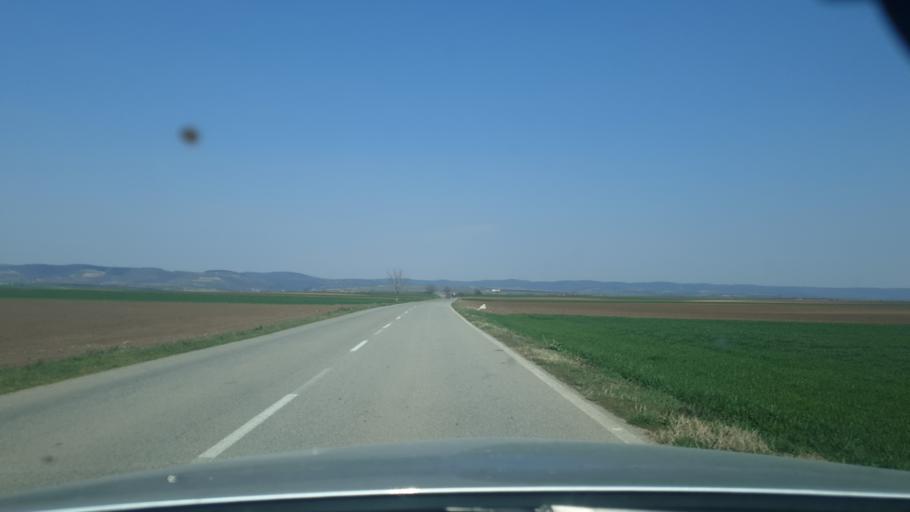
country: RS
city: Vrdnik
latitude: 45.0577
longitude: 19.7668
